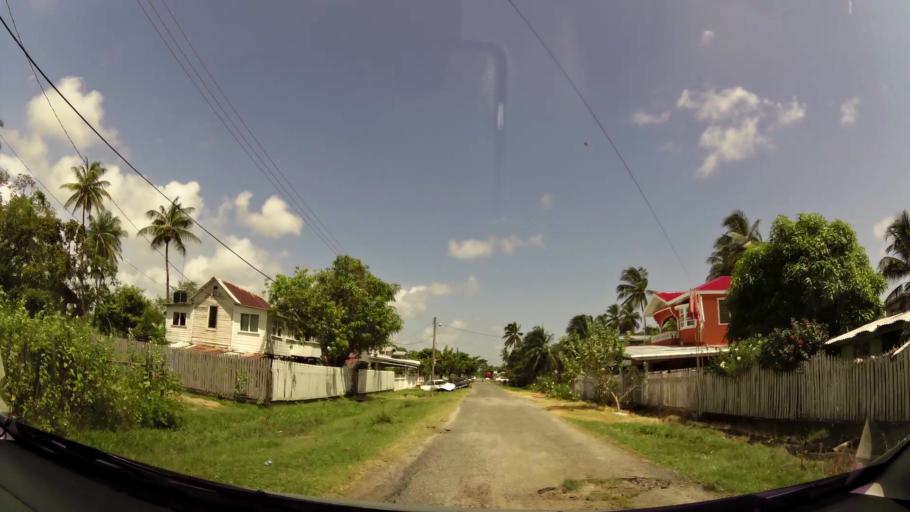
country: GY
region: Demerara-Mahaica
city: Mahaica Village
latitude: 6.7678
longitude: -58.0082
